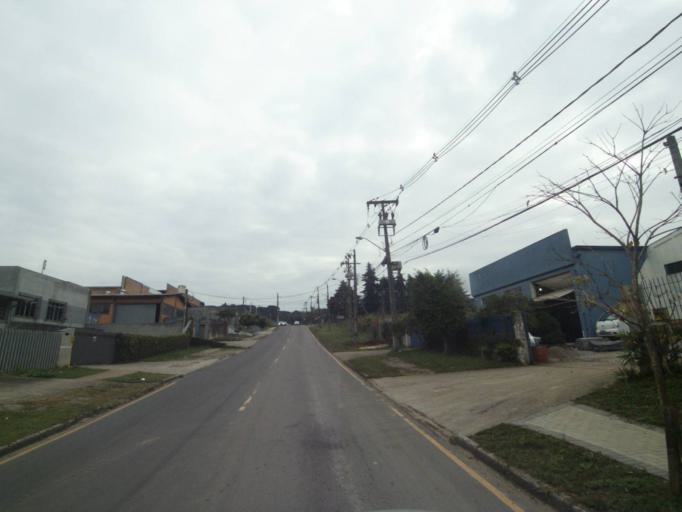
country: BR
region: Parana
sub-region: Curitiba
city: Curitiba
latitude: -25.5159
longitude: -49.3169
